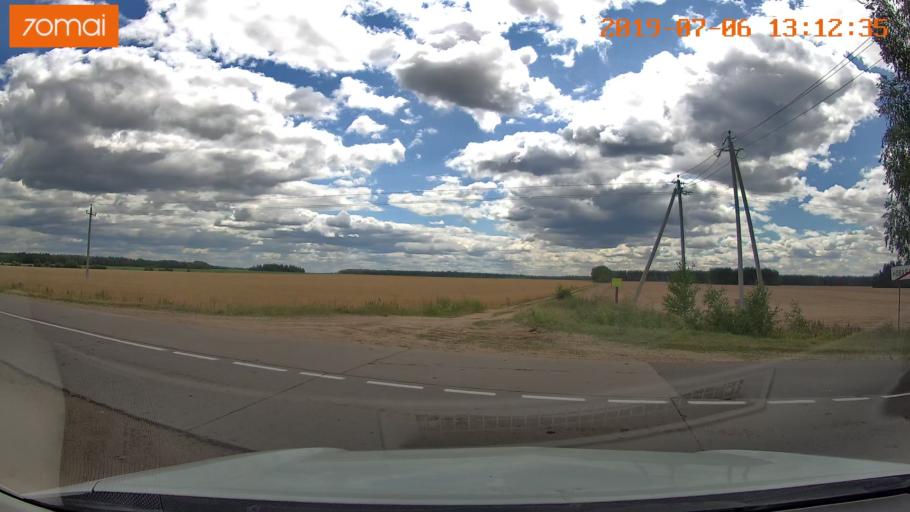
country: BY
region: Minsk
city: Enyerhyetykaw
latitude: 53.6583
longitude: 26.9936
